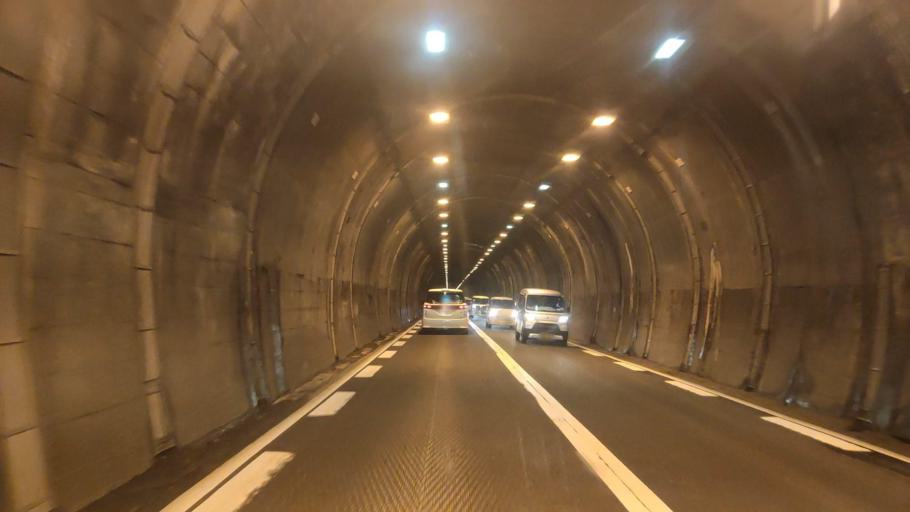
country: JP
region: Fukui
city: Takefu
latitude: 35.7834
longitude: 136.1013
